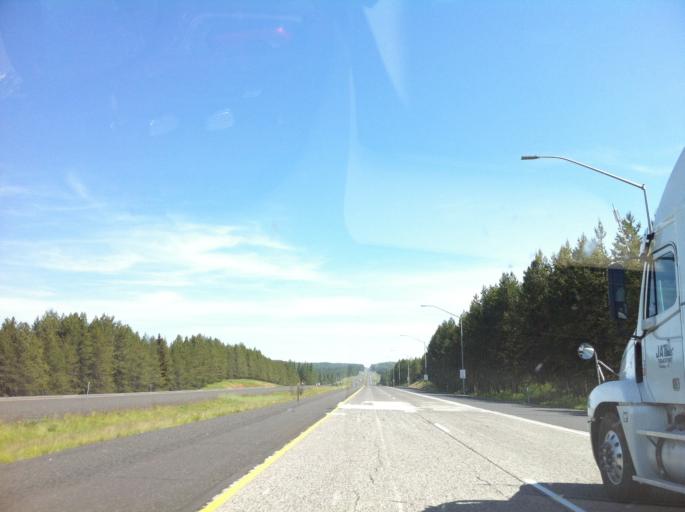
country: US
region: Oregon
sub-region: Umatilla County
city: Mission
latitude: 45.5212
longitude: -118.4398
